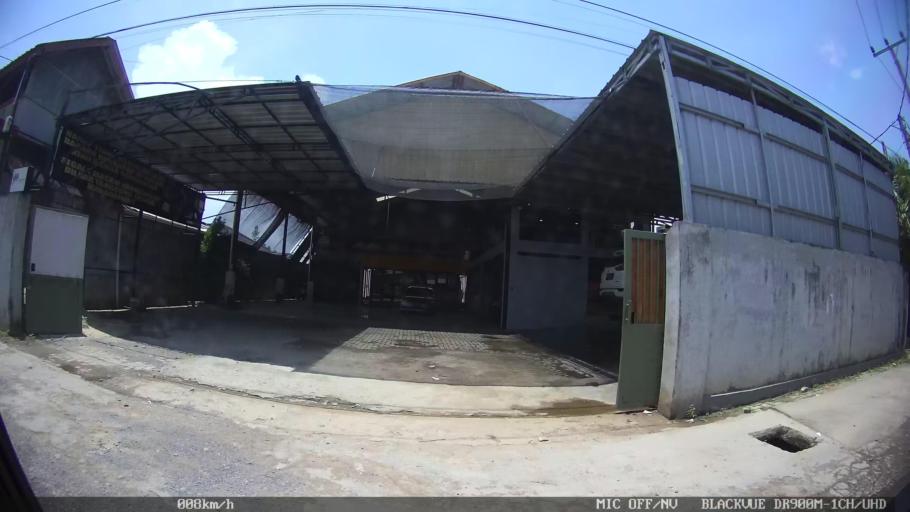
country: ID
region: Lampung
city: Kedaton
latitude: -5.3781
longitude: 105.2943
